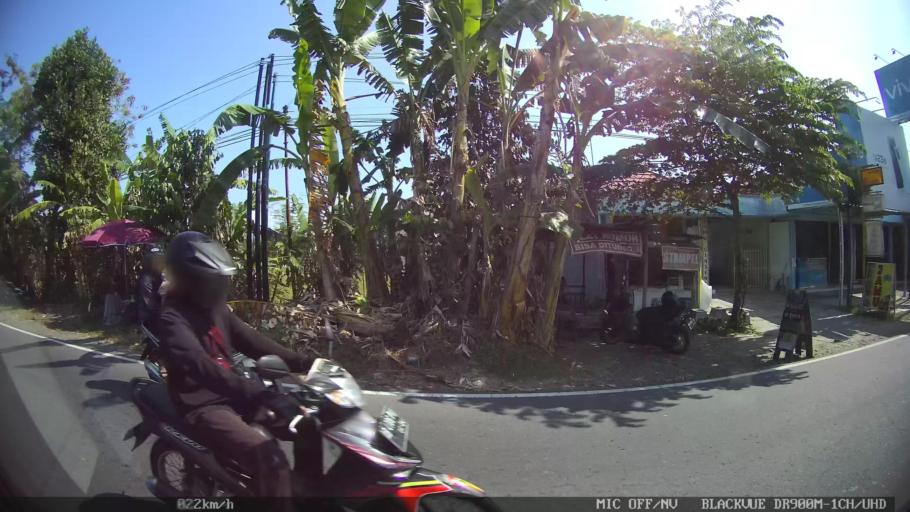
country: ID
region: Daerah Istimewa Yogyakarta
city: Sewon
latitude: -7.9140
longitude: 110.3732
